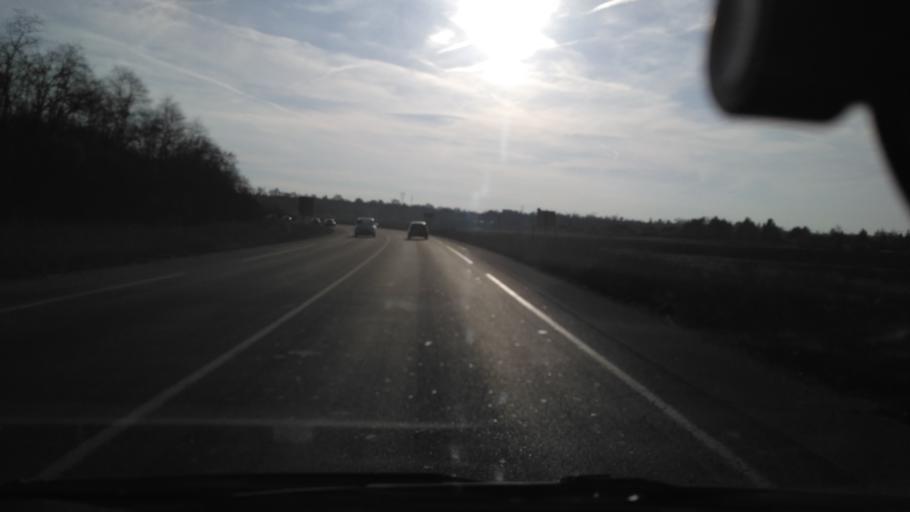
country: FR
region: Rhone-Alpes
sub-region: Departement de la Drome
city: Bourg-de-Peage
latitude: 45.0342
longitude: 5.0807
